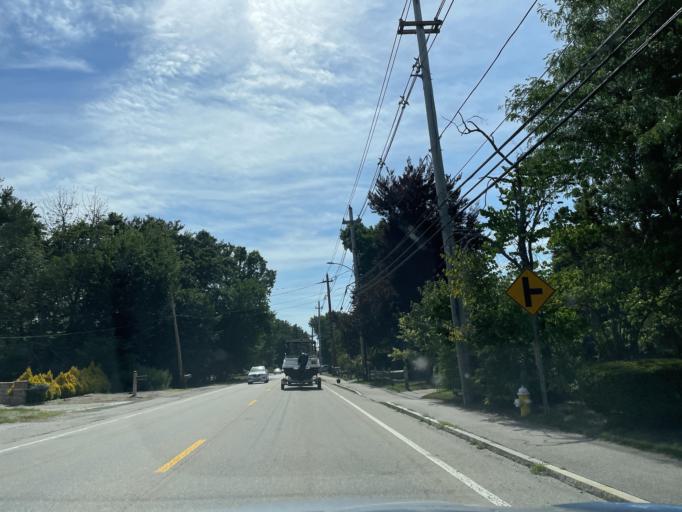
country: US
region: Massachusetts
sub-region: Norfolk County
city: Wrentham
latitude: 42.0742
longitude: -71.3395
